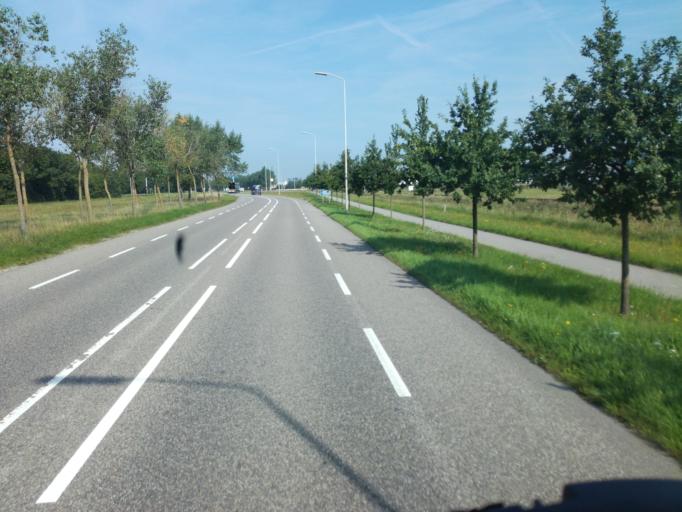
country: NL
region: North Brabant
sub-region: Gemeente Moerdijk
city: Klundert
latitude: 51.6671
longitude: 4.5609
